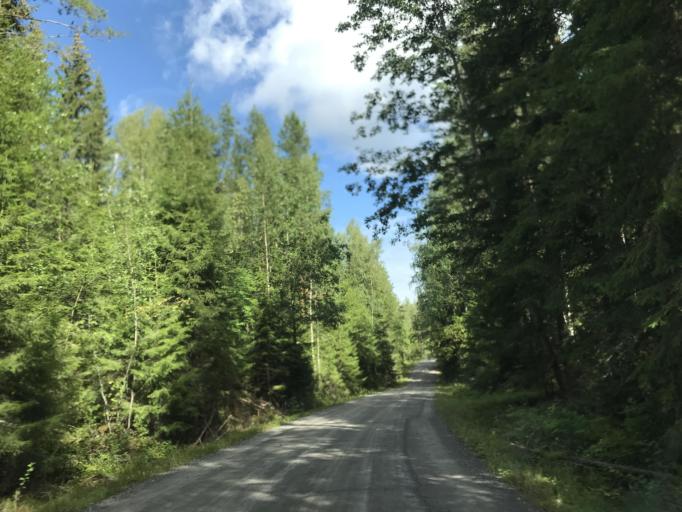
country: FI
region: Uusimaa
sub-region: Helsinki
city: Kaerkoelae
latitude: 60.6315
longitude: 23.7746
